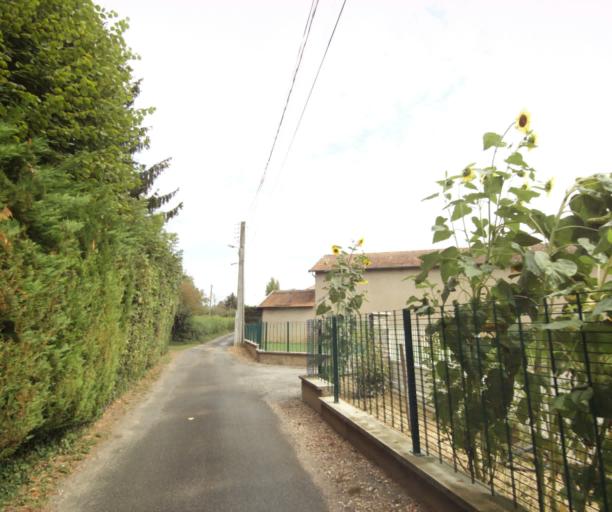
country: FR
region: Bourgogne
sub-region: Departement de Saone-et-Loire
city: Tournus
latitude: 46.5570
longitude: 4.9047
